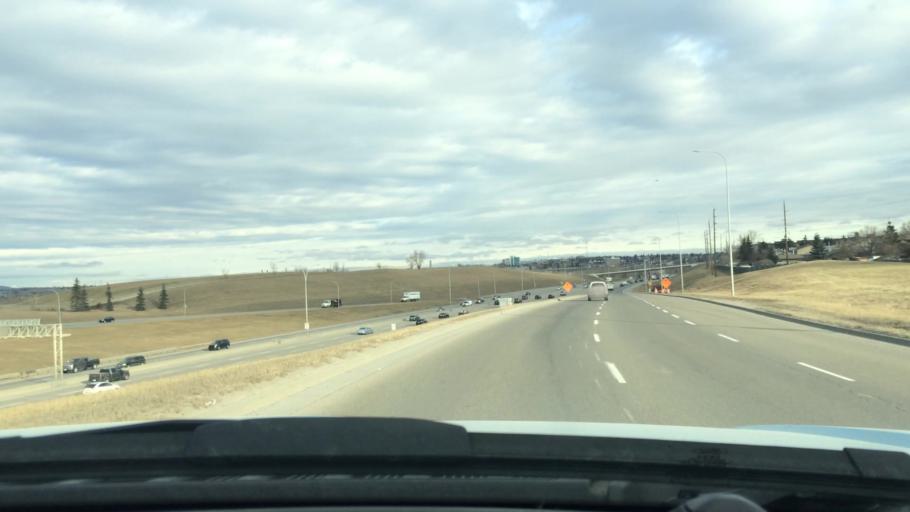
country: CA
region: Alberta
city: Calgary
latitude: 51.0166
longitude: -114.0031
